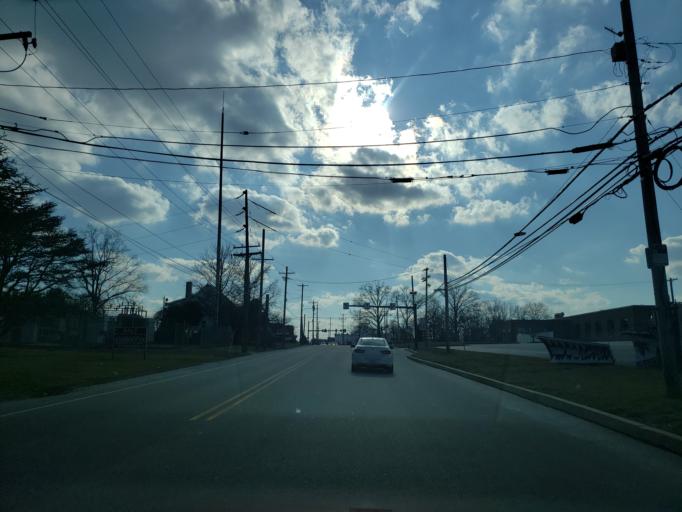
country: US
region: Pennsylvania
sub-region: Montgomery County
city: Norristown
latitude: 40.1360
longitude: -75.3312
